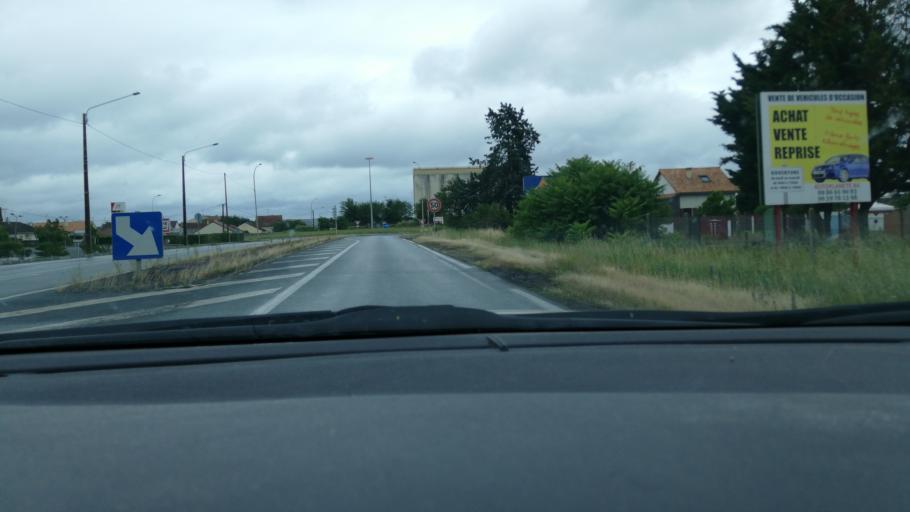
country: FR
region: Poitou-Charentes
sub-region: Departement de la Vienne
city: Naintre
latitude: 46.7557
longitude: 0.4860
